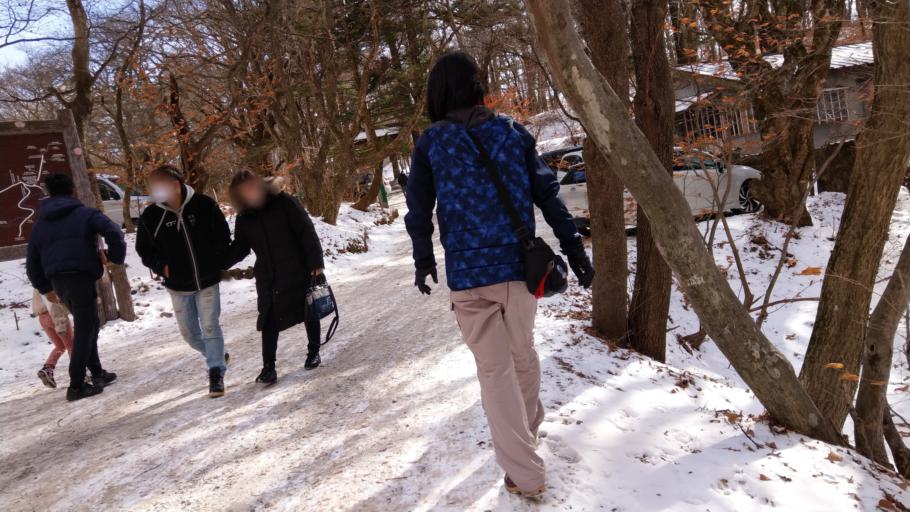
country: JP
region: Nagano
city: Komoro
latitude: 36.3688
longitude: 138.6563
